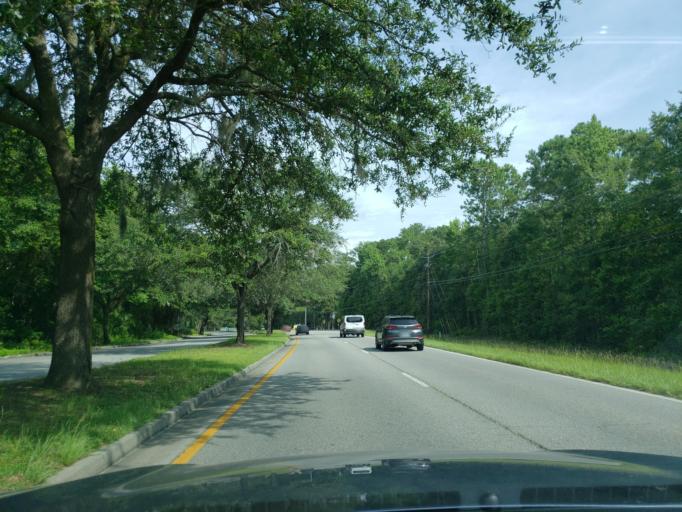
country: US
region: Georgia
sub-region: Chatham County
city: Whitemarsh Island
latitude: 32.0336
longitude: -81.0066
